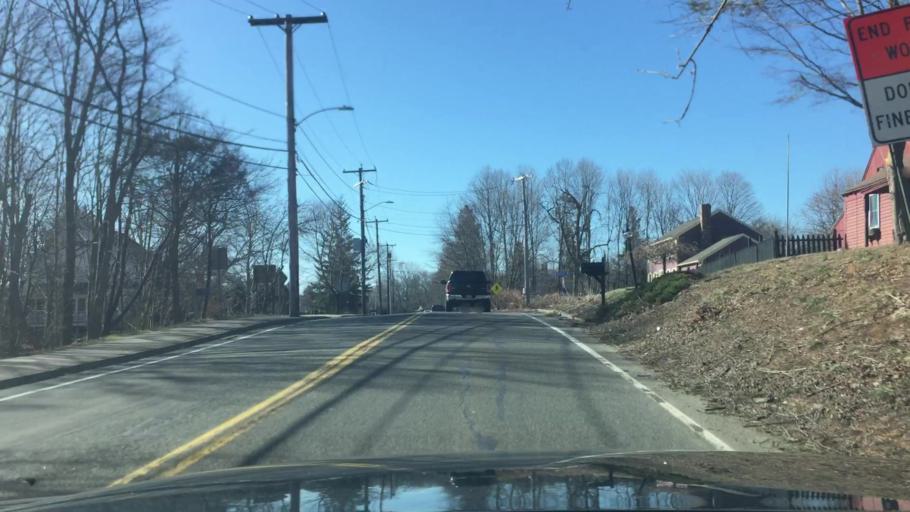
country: US
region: Massachusetts
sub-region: Norfolk County
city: Medway
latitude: 42.1510
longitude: -71.4087
